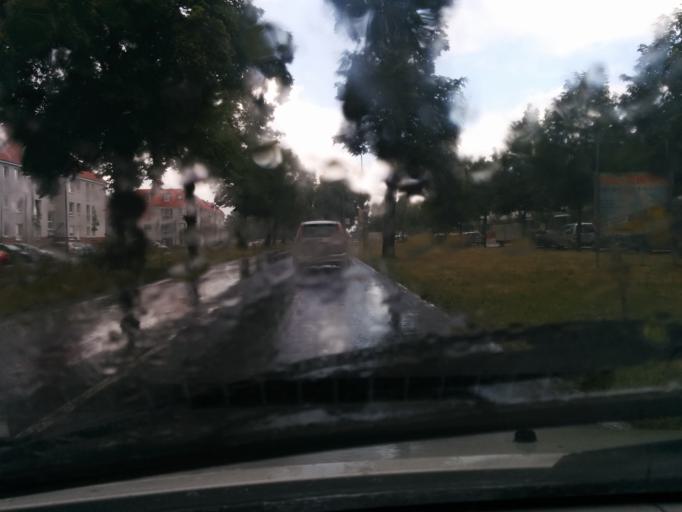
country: DE
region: Berlin
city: Staaken
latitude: 52.5586
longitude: 13.1338
